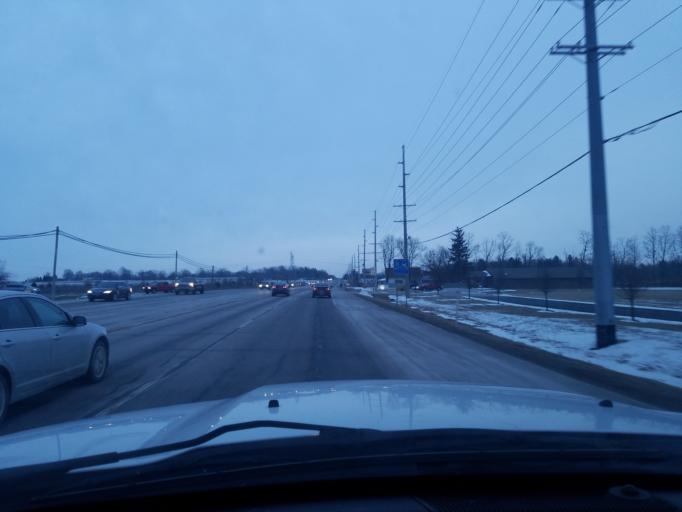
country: US
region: Indiana
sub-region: Delaware County
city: Muncie
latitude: 40.1933
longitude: -85.3292
